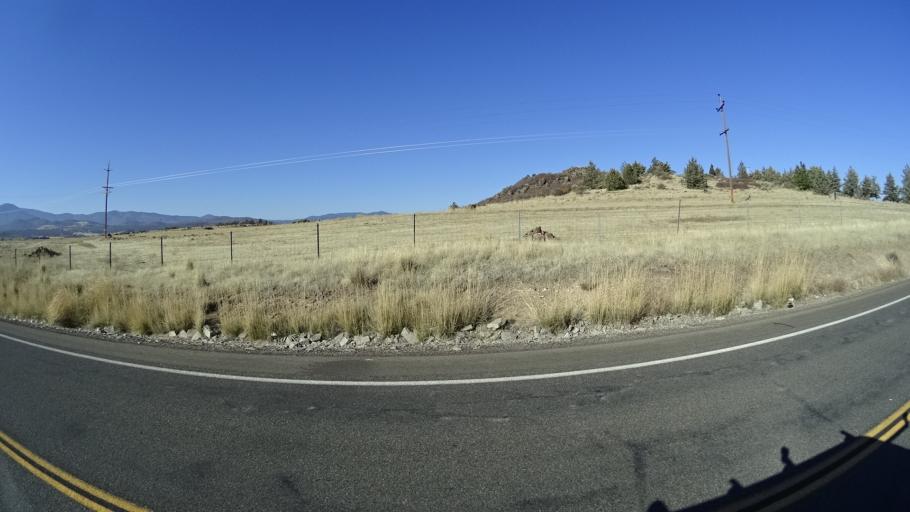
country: US
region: California
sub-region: Siskiyou County
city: Montague
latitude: 41.7116
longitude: -122.5367
